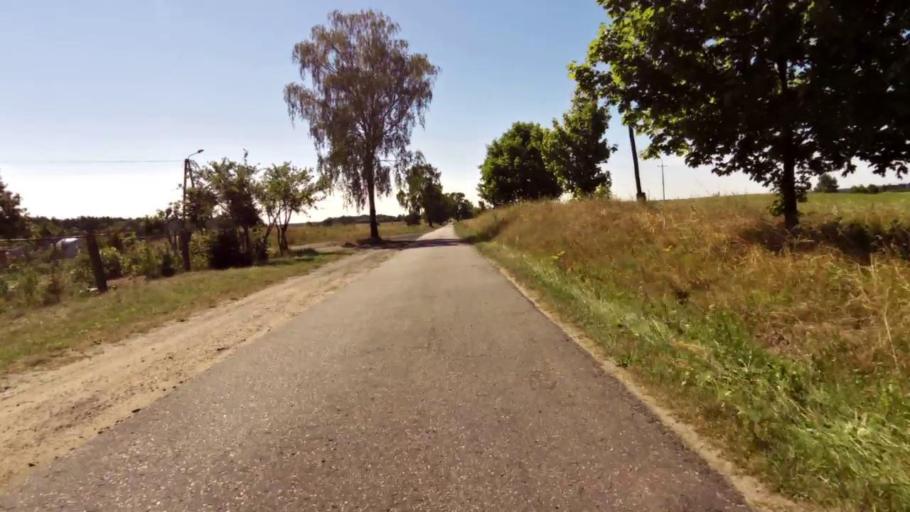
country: PL
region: West Pomeranian Voivodeship
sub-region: Powiat szczecinecki
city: Szczecinek
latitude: 53.7030
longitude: 16.6197
